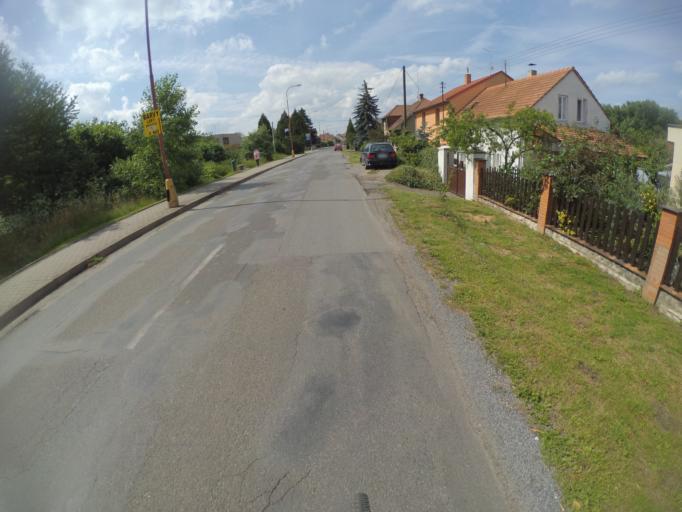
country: CZ
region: Central Bohemia
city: Libis
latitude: 50.2665
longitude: 14.5088
